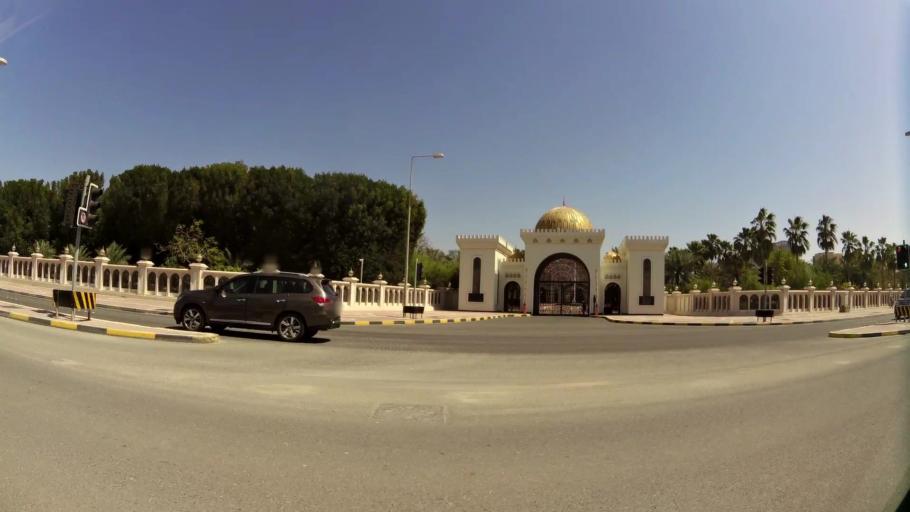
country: BH
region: Manama
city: Manama
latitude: 26.2188
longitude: 50.5901
